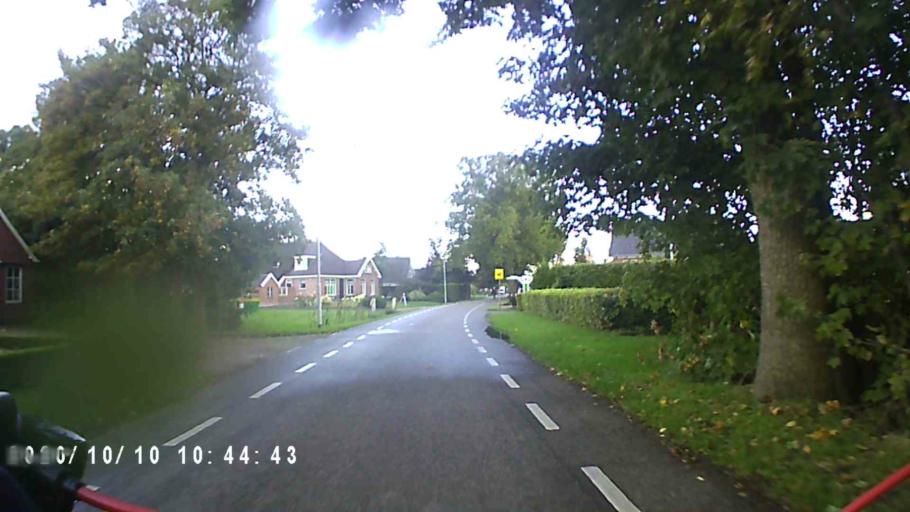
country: NL
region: Groningen
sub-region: Gemeente Grootegast
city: Grootegast
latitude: 53.1717
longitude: 6.2605
